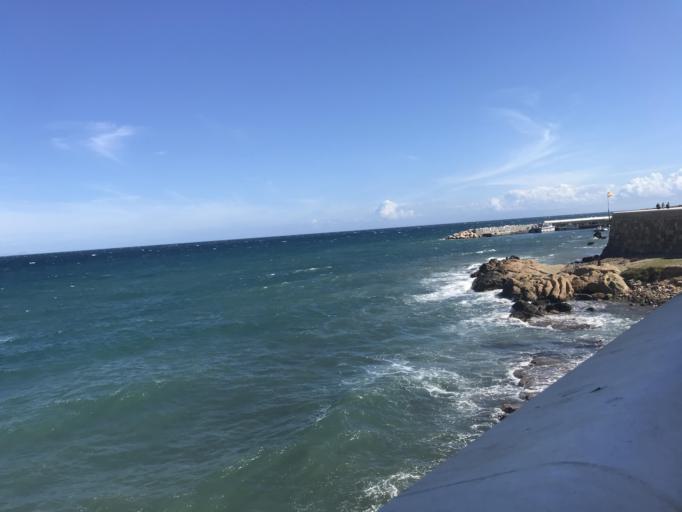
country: ES
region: Valencia
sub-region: Provincia de Alicante
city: Santa Pola
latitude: 38.1673
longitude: -0.4822
